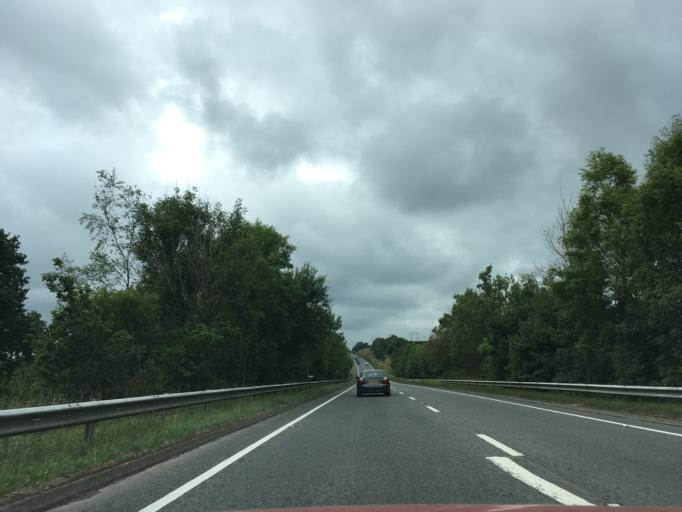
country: GB
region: Wales
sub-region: Carmarthenshire
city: Whitland
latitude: 51.8239
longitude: -4.5827
